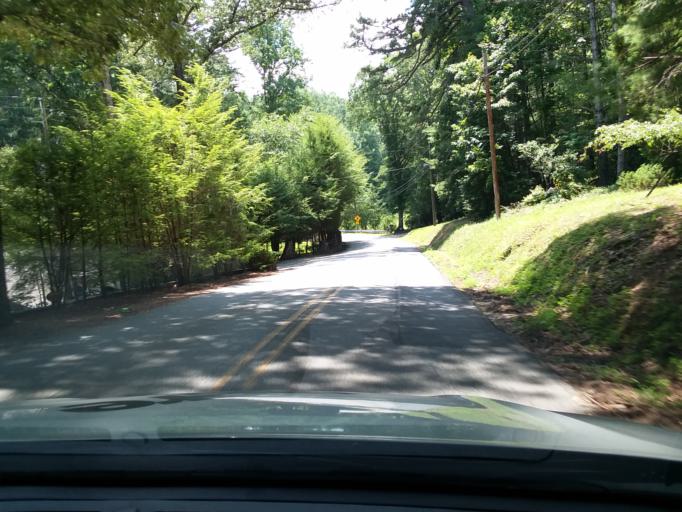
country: US
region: Georgia
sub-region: Rabun County
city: Clayton
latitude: 34.7732
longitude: -83.4331
